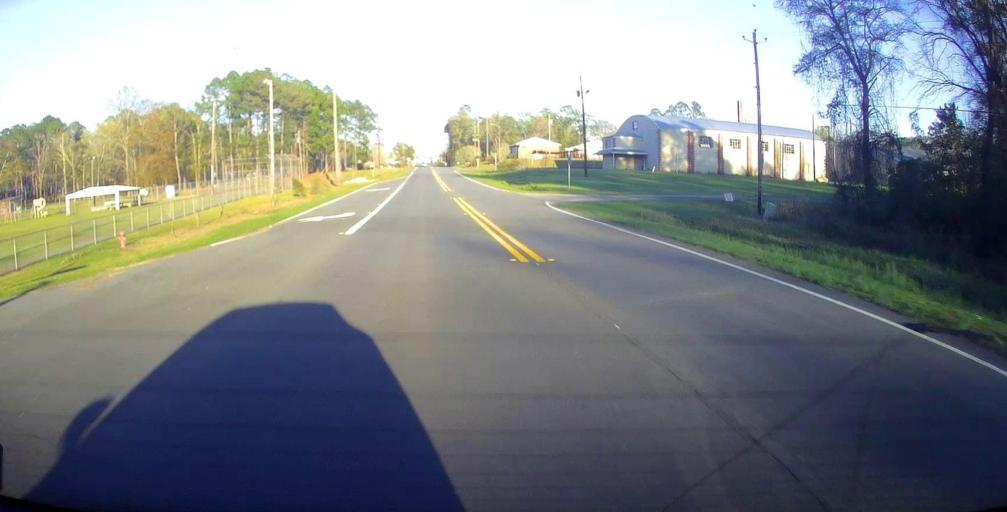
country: US
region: Georgia
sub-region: Wilcox County
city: Abbeville
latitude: 31.9924
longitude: -83.3148
